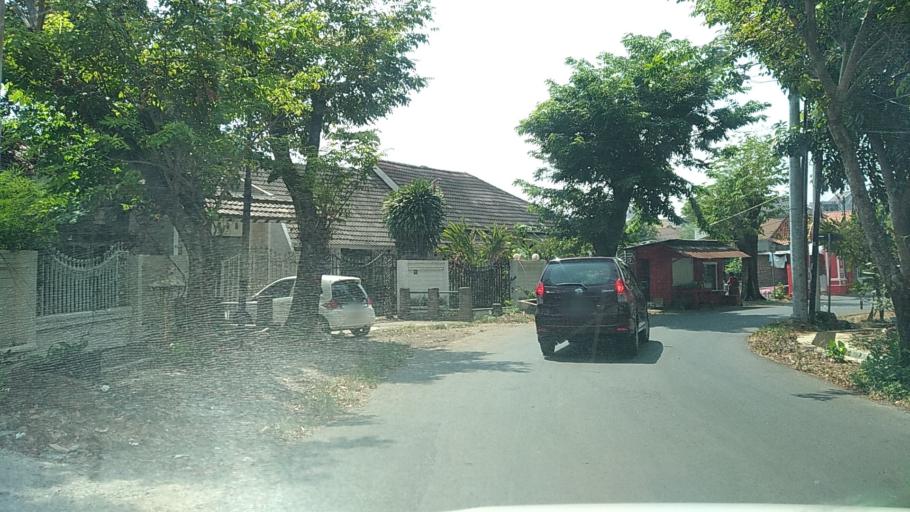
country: ID
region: Central Java
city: Semarang
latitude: -7.0097
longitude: 110.4129
